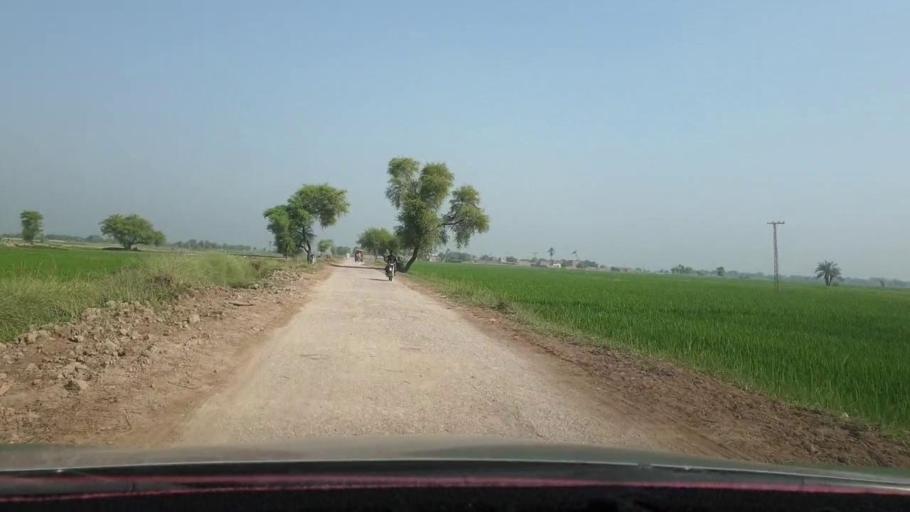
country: PK
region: Sindh
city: Kambar
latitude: 27.5969
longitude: 67.9368
